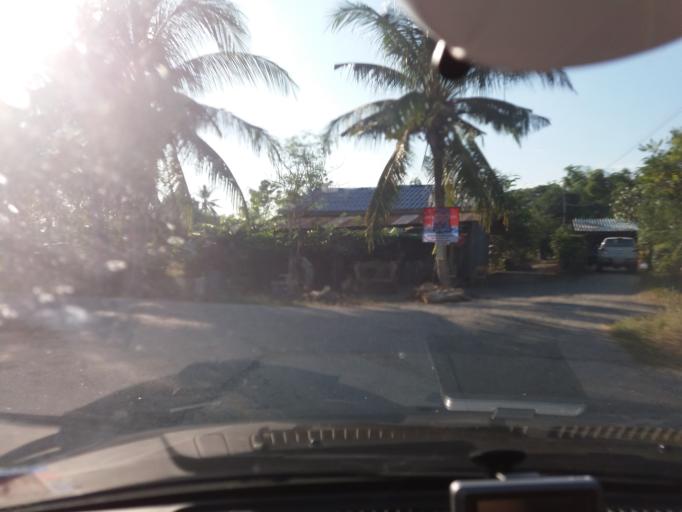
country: TH
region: Suphan Buri
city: Doem Bang Nang Buat
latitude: 14.9131
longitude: 100.1315
